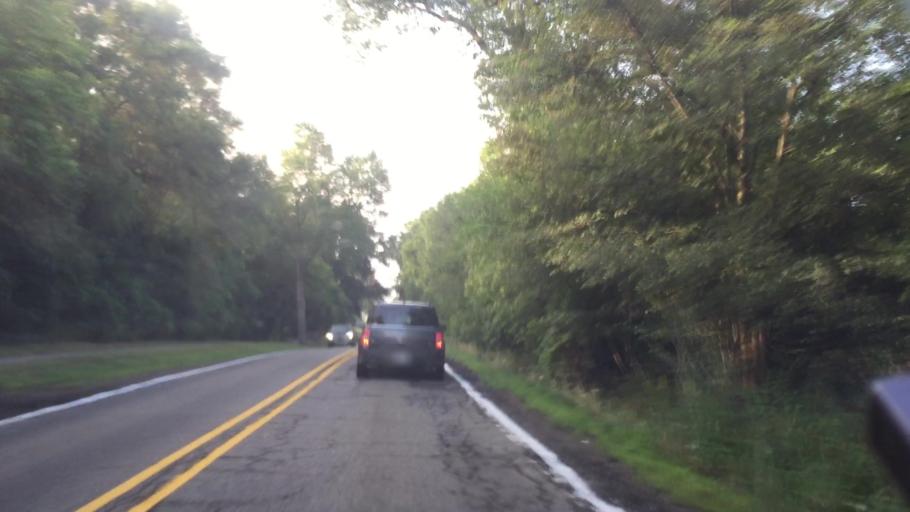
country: US
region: Michigan
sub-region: Oakland County
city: Bloomfield Hills
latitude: 42.6020
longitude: -83.2479
